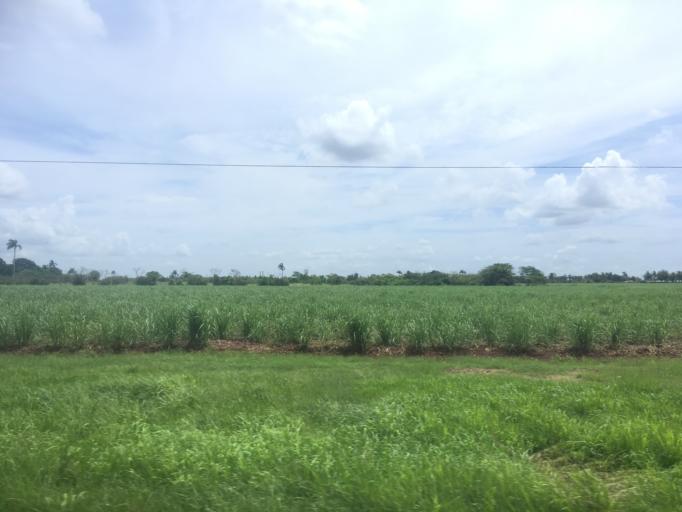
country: CU
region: Matanzas
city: Perico
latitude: 22.7810
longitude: -81.0399
